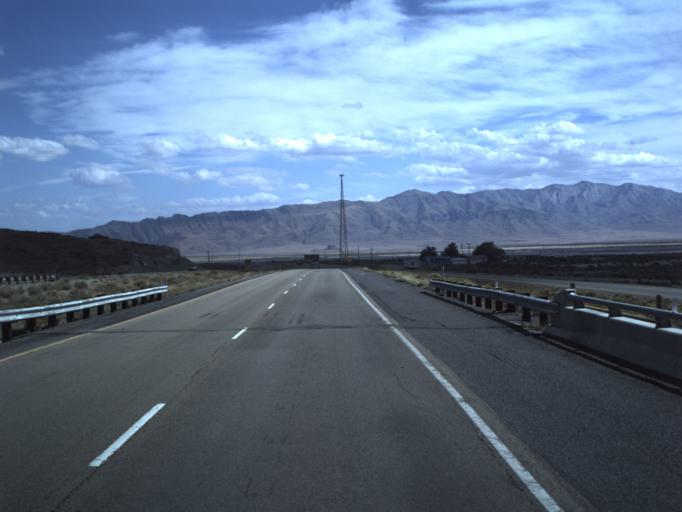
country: US
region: Utah
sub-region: Tooele County
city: Grantsville
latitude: 40.7623
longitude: -112.7809
